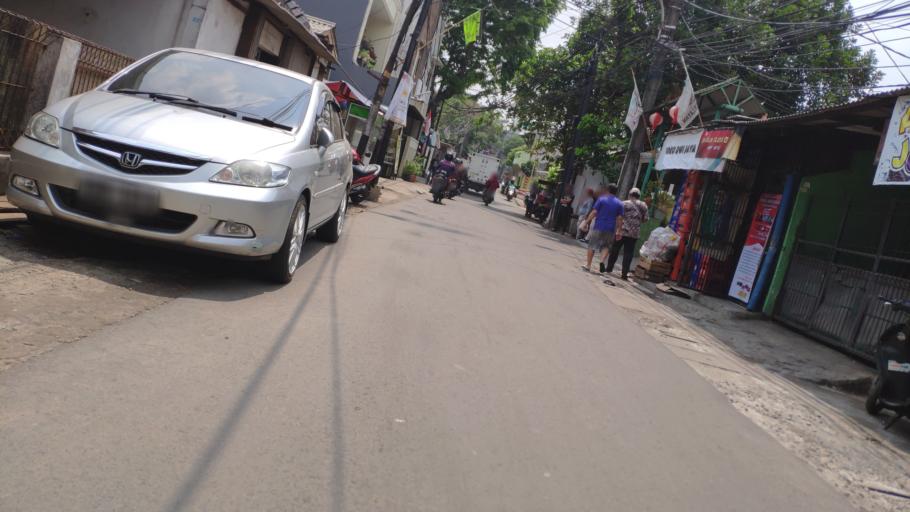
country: ID
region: Jakarta Raya
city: Jakarta
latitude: -6.3062
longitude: 106.8367
